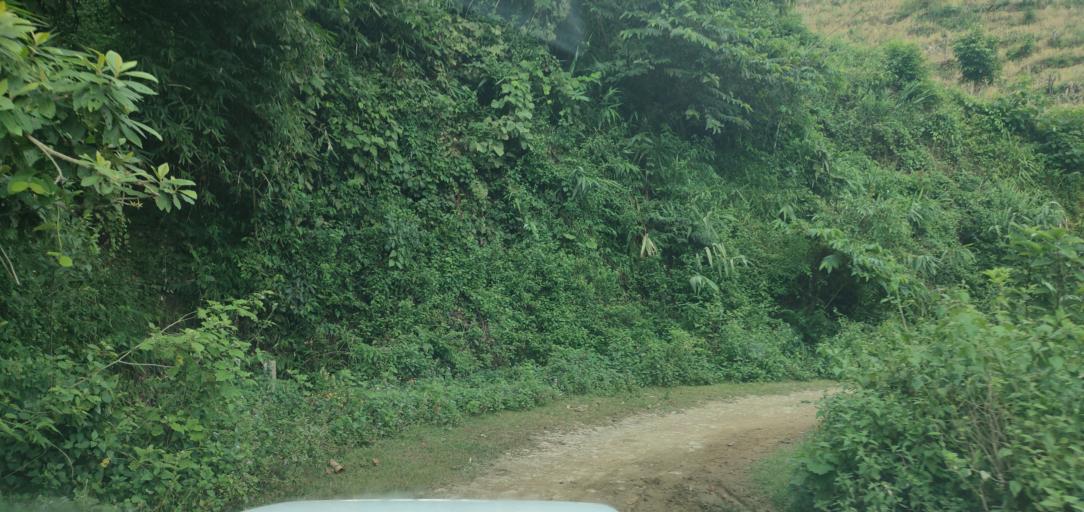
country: LA
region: Phongsali
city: Phongsali
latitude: 21.4448
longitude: 102.3160
